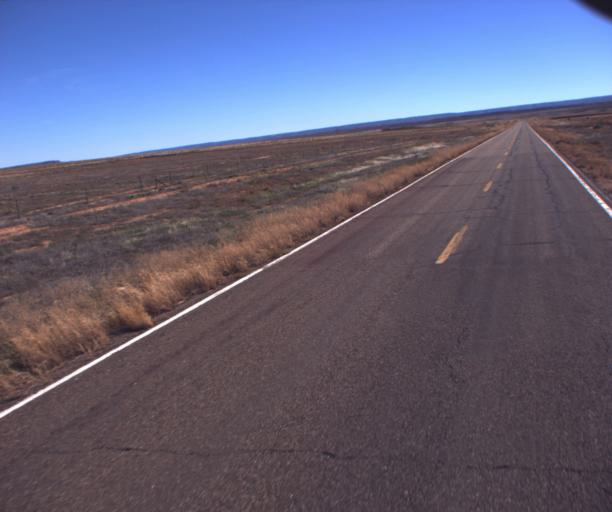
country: US
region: Arizona
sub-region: Coconino County
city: Fredonia
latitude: 36.9242
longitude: -112.4579
